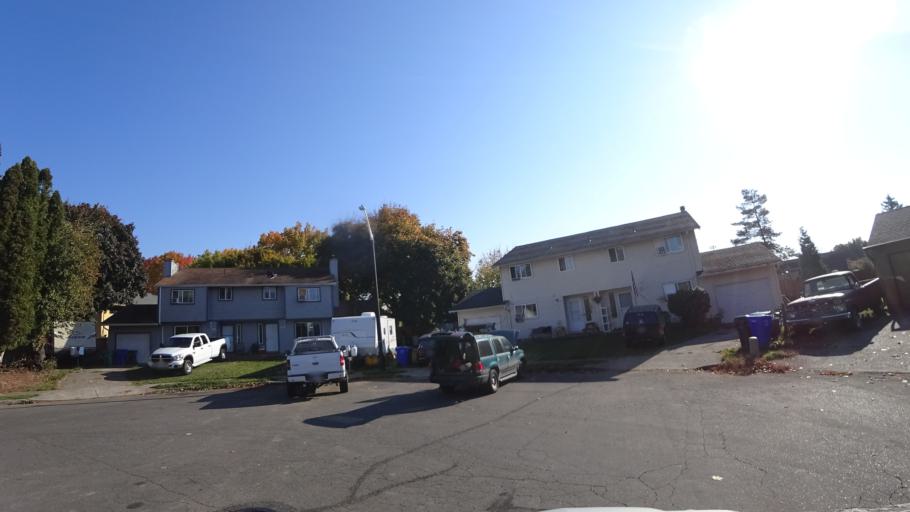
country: US
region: Oregon
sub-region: Multnomah County
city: Gresham
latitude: 45.5093
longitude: -122.4279
